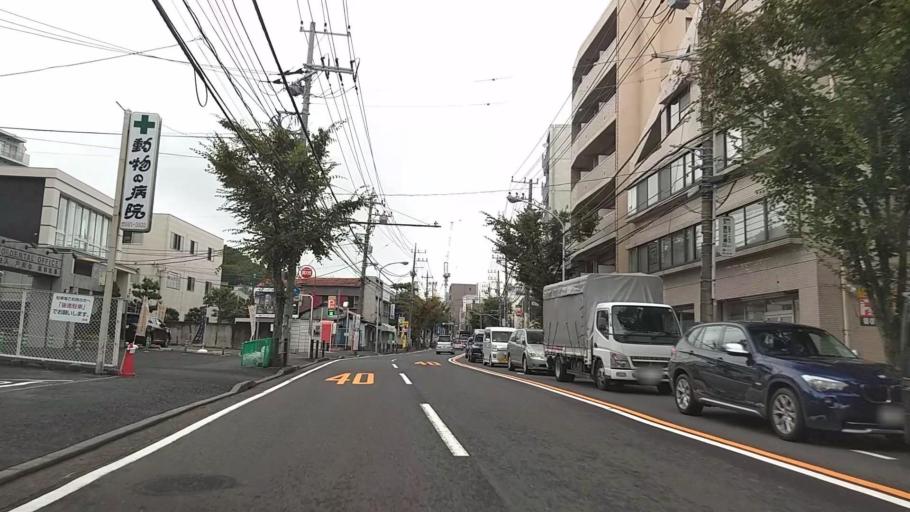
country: JP
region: Kanagawa
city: Fujisawa
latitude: 35.3960
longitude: 139.5302
